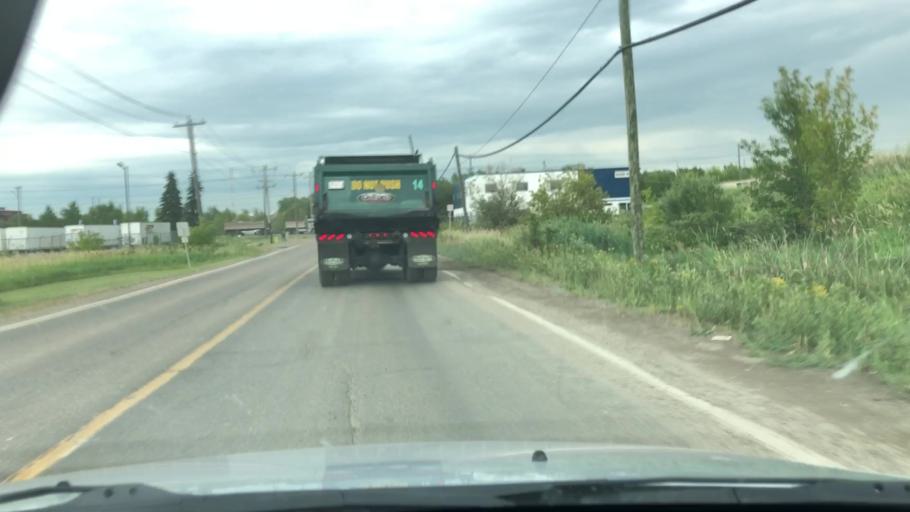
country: CA
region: Alberta
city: Edmonton
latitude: 53.5267
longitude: -113.3966
